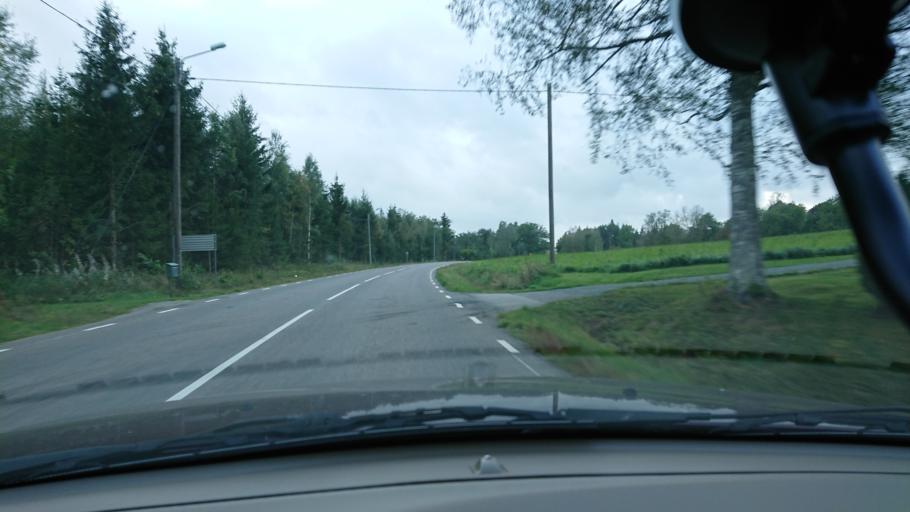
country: SE
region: Kronoberg
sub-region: Vaxjo Kommun
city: Lammhult
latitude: 57.0896
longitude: 14.6468
